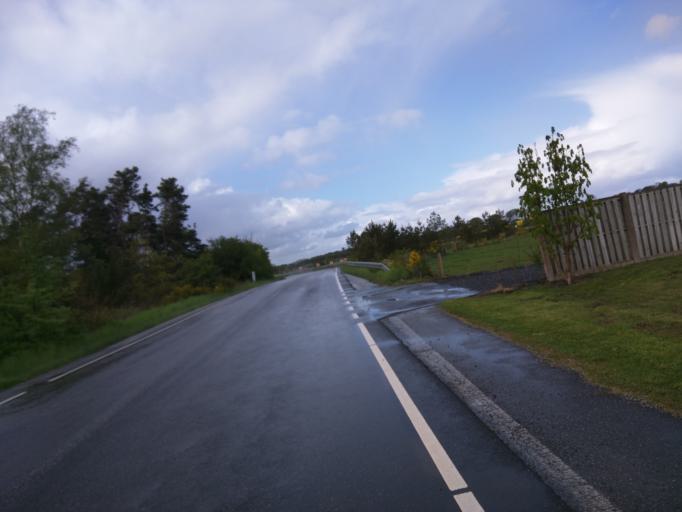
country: DK
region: Central Jutland
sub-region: Viborg Kommune
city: Viborg
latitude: 56.3893
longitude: 9.4452
